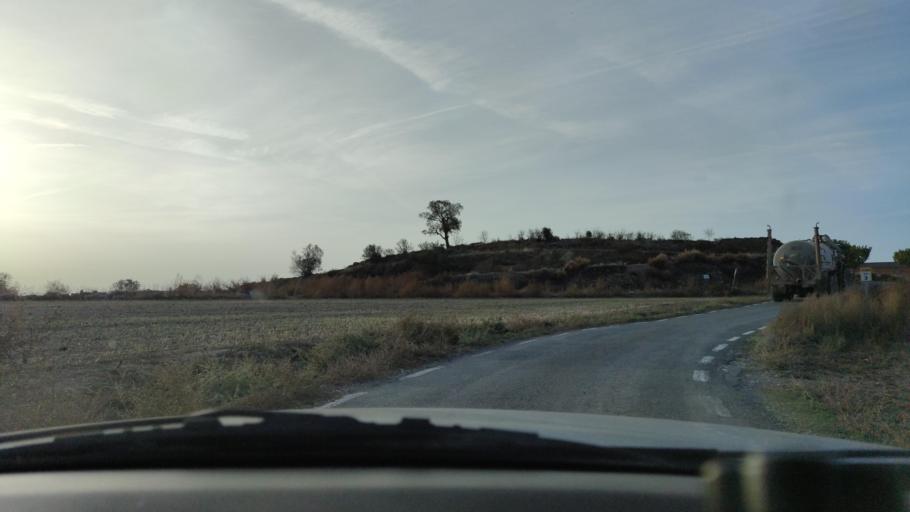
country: ES
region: Catalonia
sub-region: Provincia de Lleida
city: Agramunt
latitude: 41.8374
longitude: 1.0951
